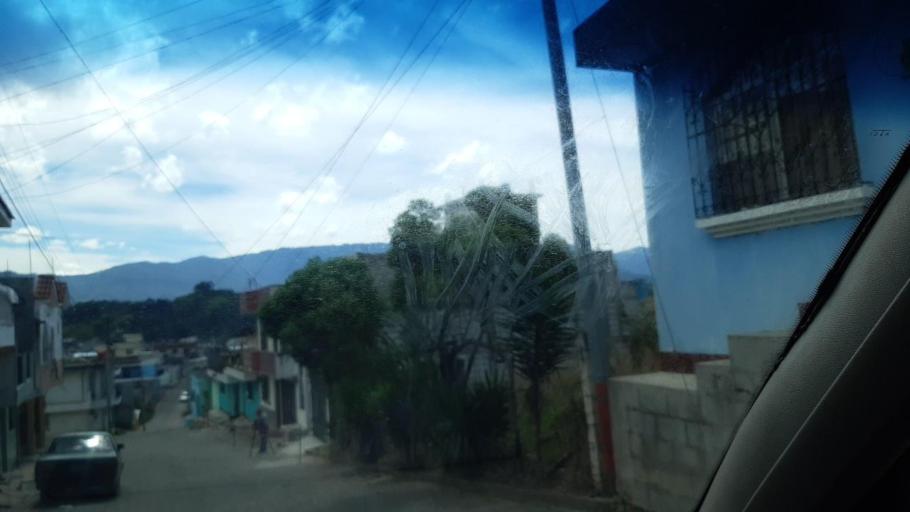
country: GT
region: Quetzaltenango
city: Salcaja
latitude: 14.8798
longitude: -91.4633
